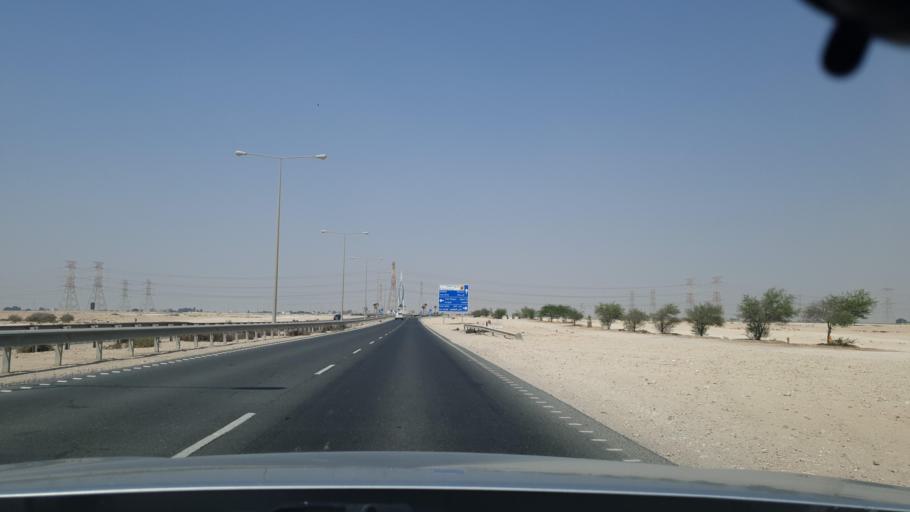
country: QA
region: Al Khawr
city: Al Khawr
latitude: 25.7501
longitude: 51.4784
